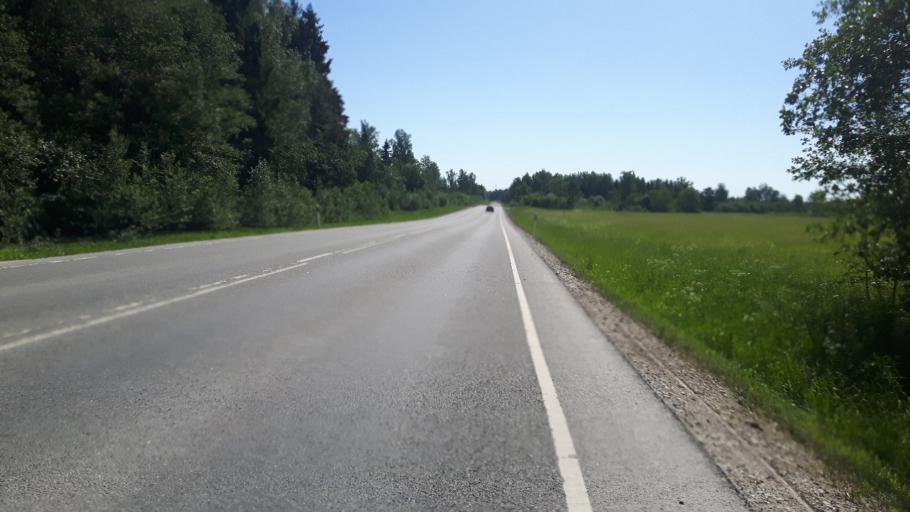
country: EE
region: Raplamaa
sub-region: Rapla vald
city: Rapla
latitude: 59.0347
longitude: 24.8286
